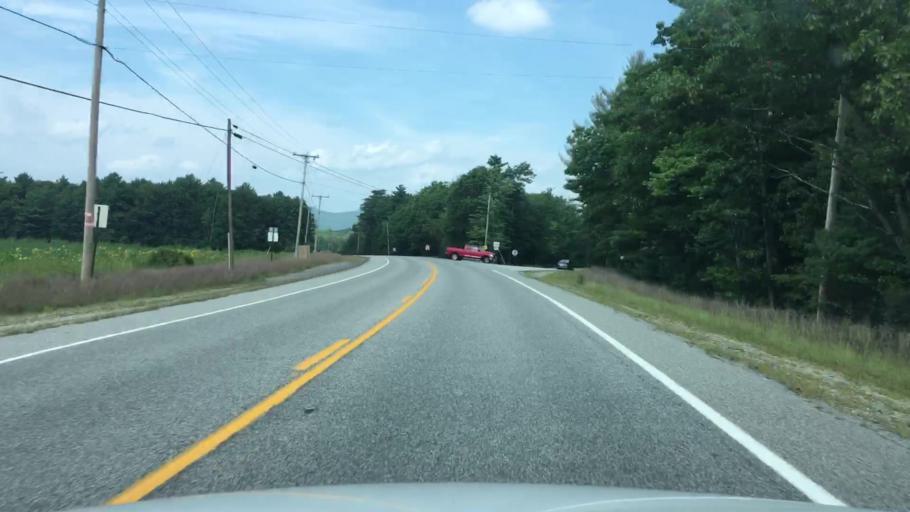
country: US
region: Maine
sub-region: Oxford County
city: Canton
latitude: 44.4653
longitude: -70.3214
